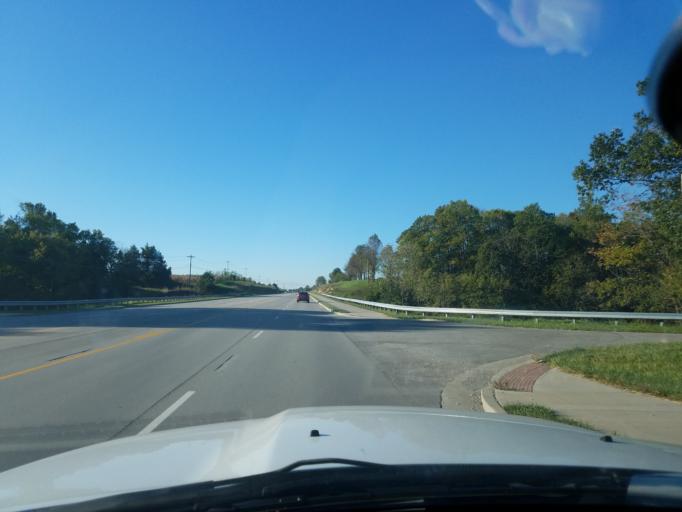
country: US
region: Kentucky
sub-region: Nelson County
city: Bardstown
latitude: 37.8106
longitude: -85.4284
